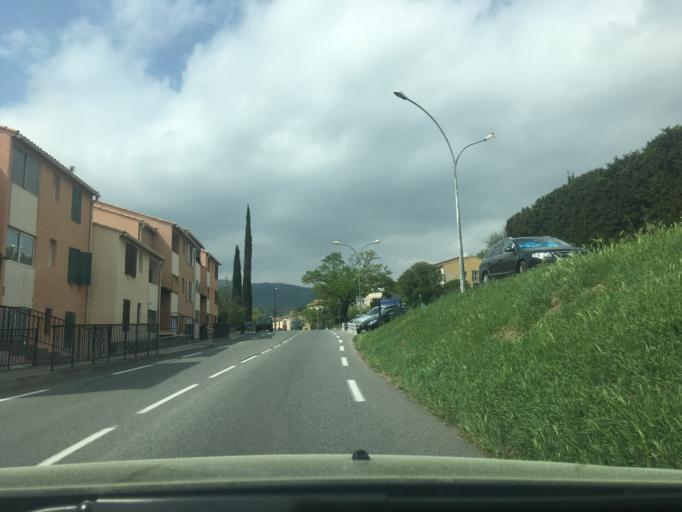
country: FR
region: Provence-Alpes-Cote d'Azur
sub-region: Departement du Var
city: Fayence
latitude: 43.6201
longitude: 6.6922
